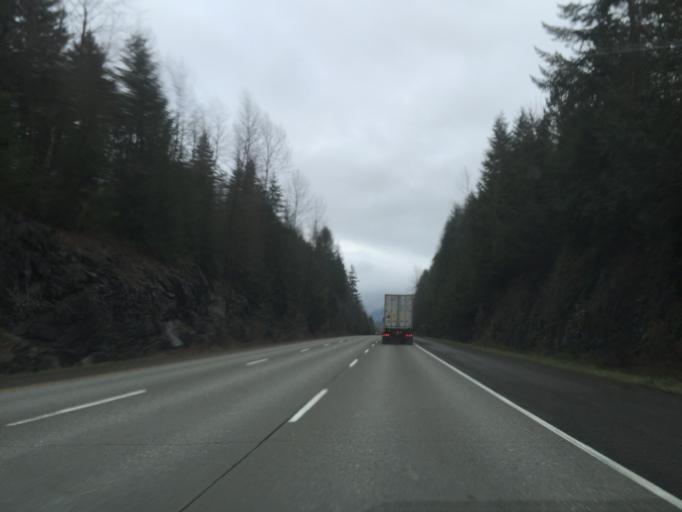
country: US
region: Washington
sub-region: King County
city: North Bend
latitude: 47.4937
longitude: -121.8094
